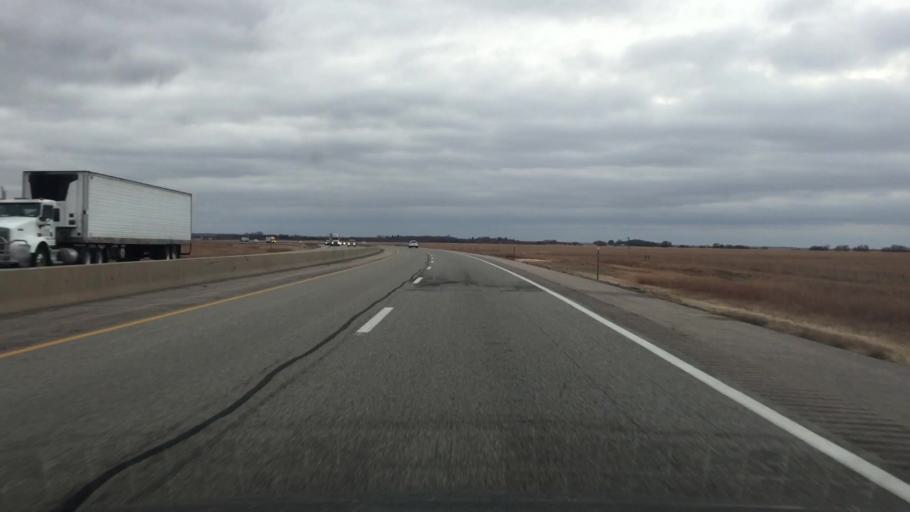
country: US
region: Kansas
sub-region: Butler County
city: El Dorado
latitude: 37.9026
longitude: -96.8284
